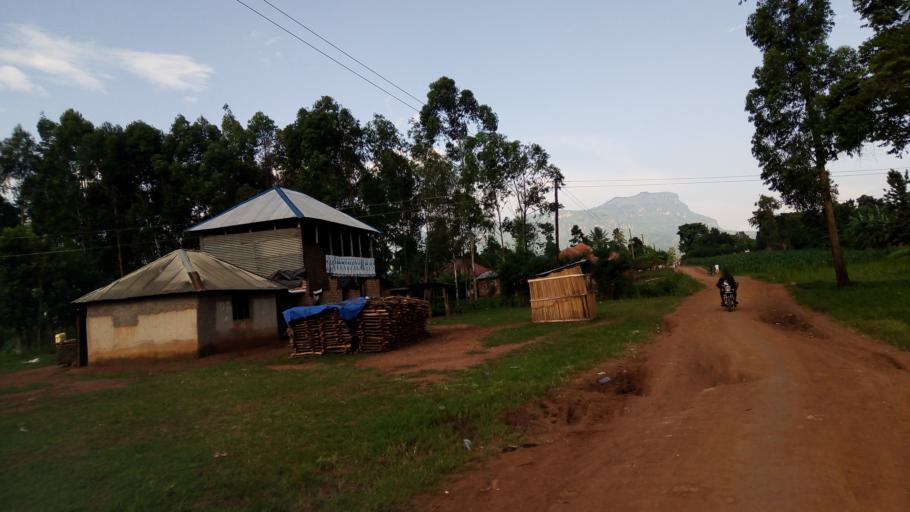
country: UG
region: Eastern Region
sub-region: Mbale District
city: Mbale
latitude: 1.0549
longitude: 34.1634
